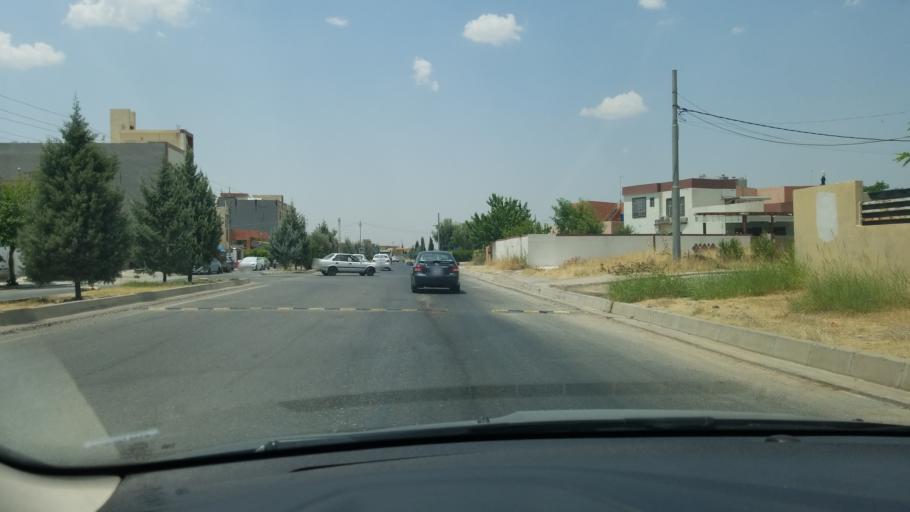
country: IQ
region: Arbil
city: Erbil
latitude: 36.1717
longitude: 44.0580
